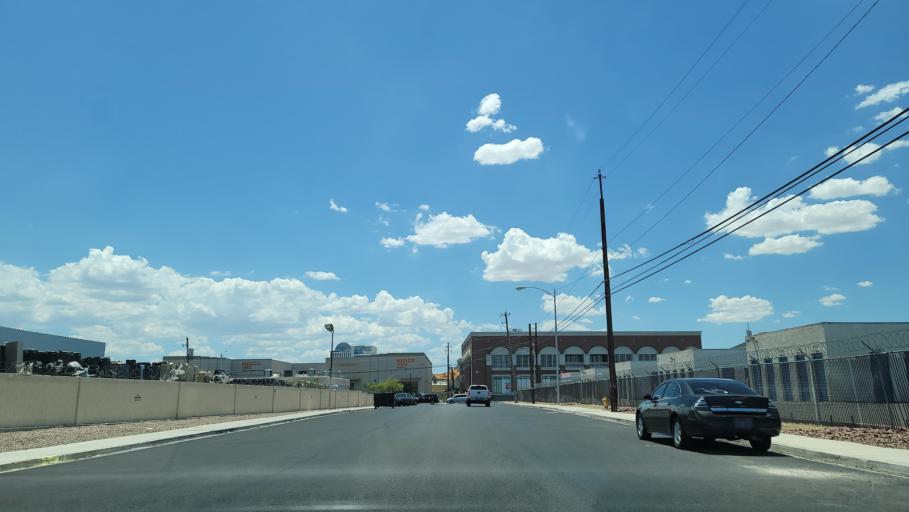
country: US
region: Nevada
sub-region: Clark County
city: Spring Valley
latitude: 36.1294
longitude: -115.1970
